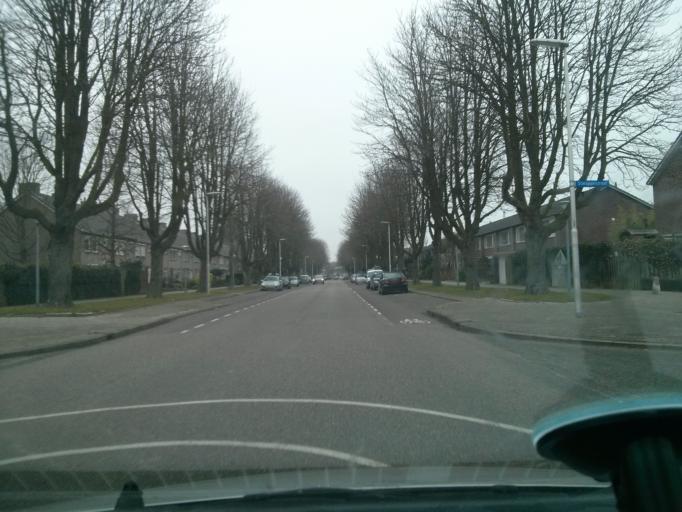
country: NL
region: North Brabant
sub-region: Gemeente Son en Breugel
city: Son
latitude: 51.4793
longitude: 5.4921
